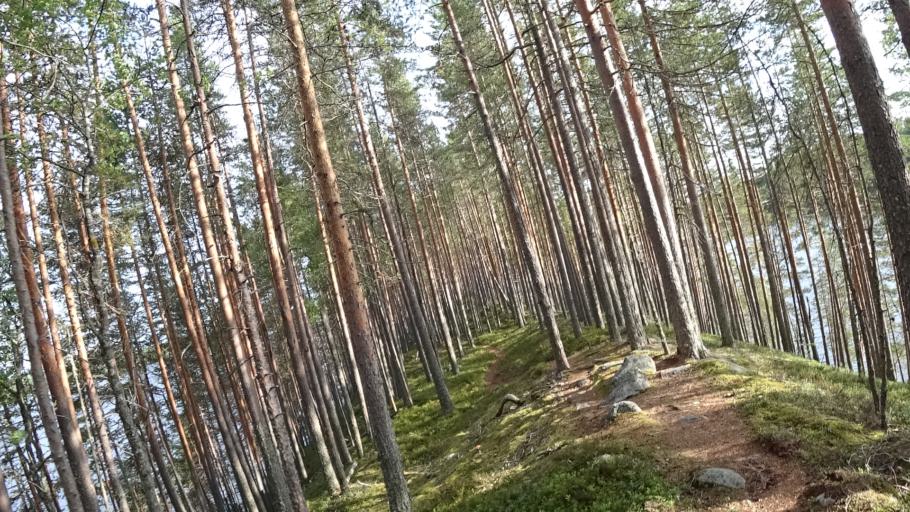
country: FI
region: North Karelia
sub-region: Joensuu
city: Ilomantsi
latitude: 62.5695
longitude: 31.1797
